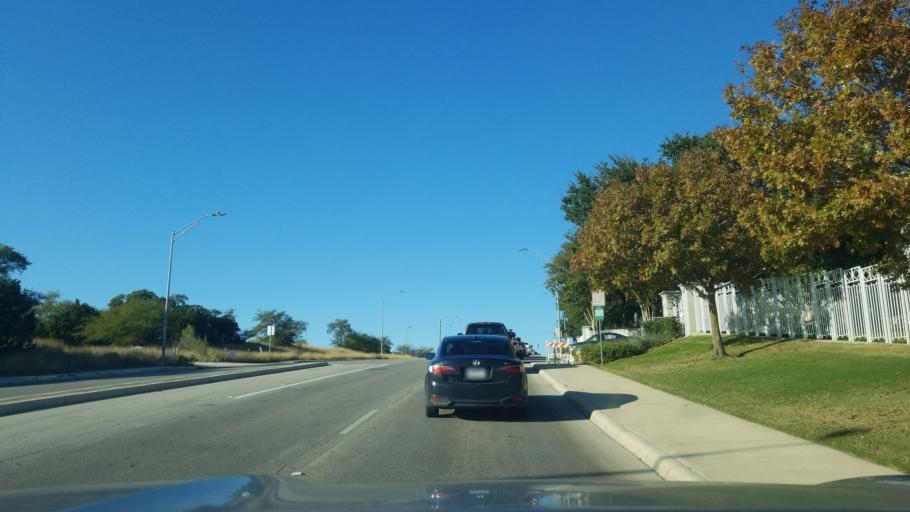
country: US
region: Texas
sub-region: Bexar County
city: Hollywood Park
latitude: 29.6406
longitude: -98.4890
